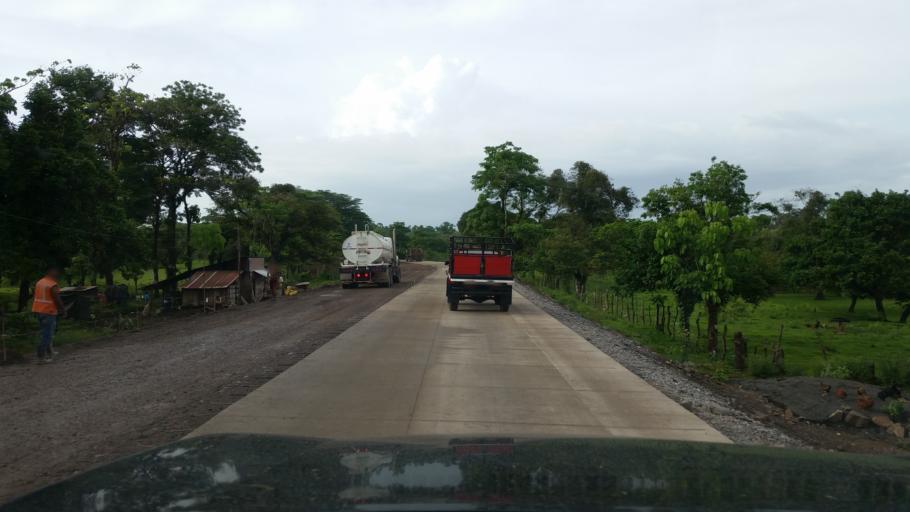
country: NI
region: Matagalpa
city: Rio Blanco
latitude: 13.0770
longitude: -85.0604
